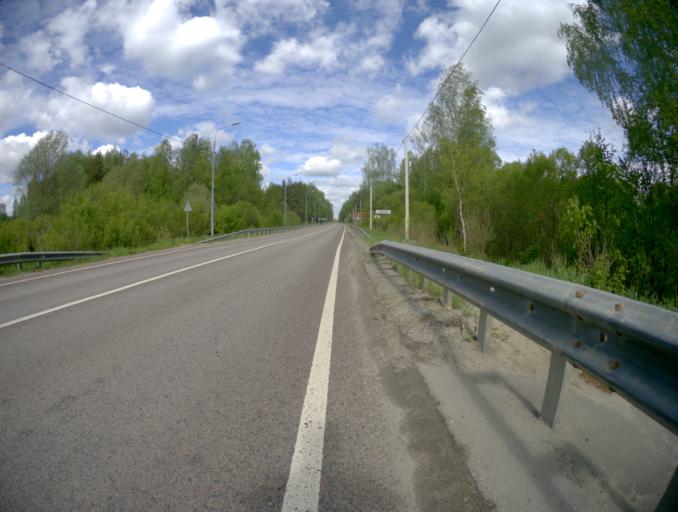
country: RU
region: Rjazan
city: Spas-Klepiki
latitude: 55.2427
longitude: 40.0512
